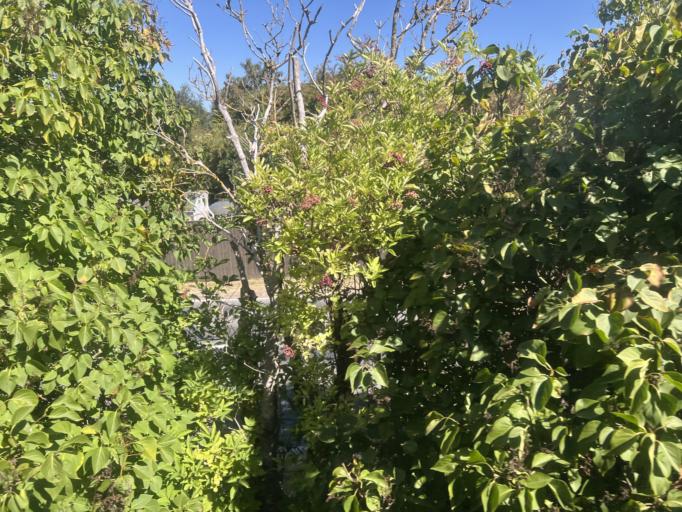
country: GB
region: England
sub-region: Lincolnshire
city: Kirton
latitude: 52.9762
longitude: -0.1224
